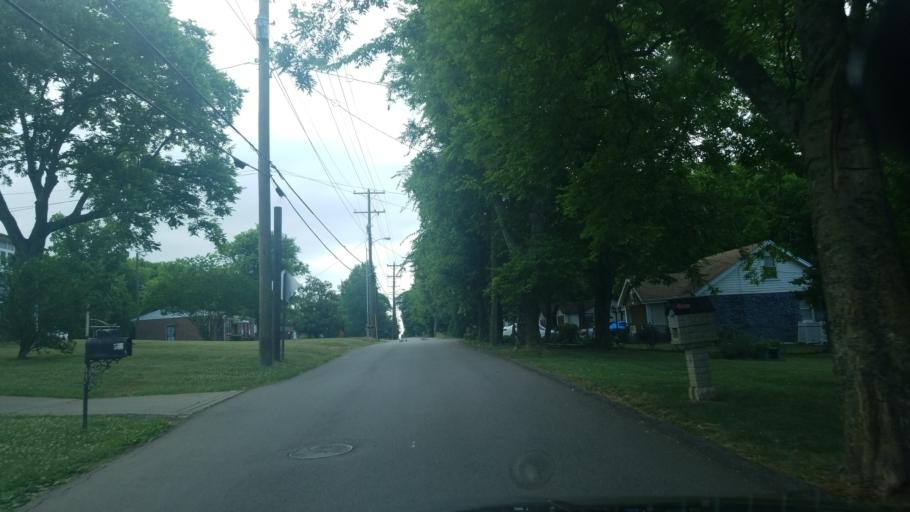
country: US
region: Tennessee
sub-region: Davidson County
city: Nashville
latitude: 36.2287
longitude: -86.7430
